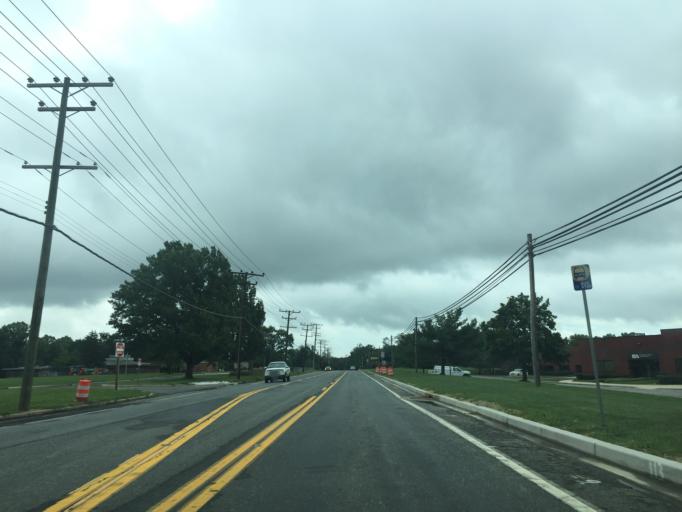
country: US
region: Maryland
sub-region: Harford County
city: Edgewood
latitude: 39.4490
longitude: -76.2972
